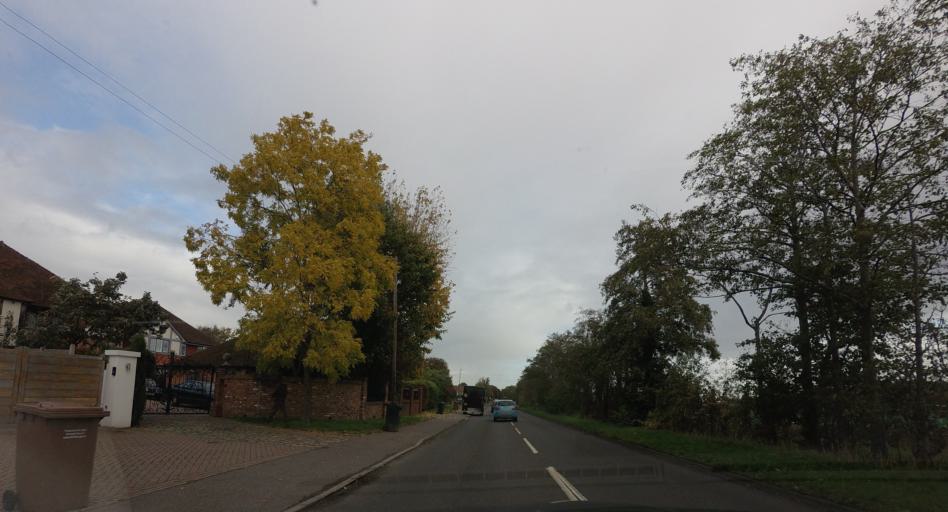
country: GB
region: England
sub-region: Kent
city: Swanley
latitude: 51.4167
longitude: 0.1684
